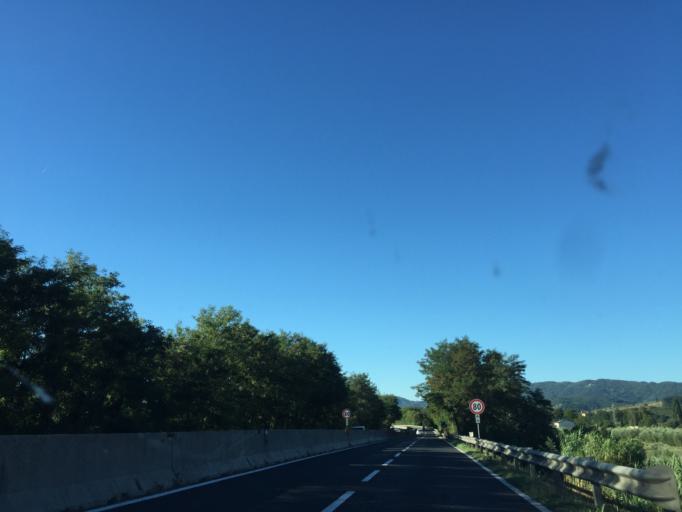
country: IT
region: Tuscany
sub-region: Provincia di Pistoia
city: Pistoia
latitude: 43.9428
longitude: 10.8941
